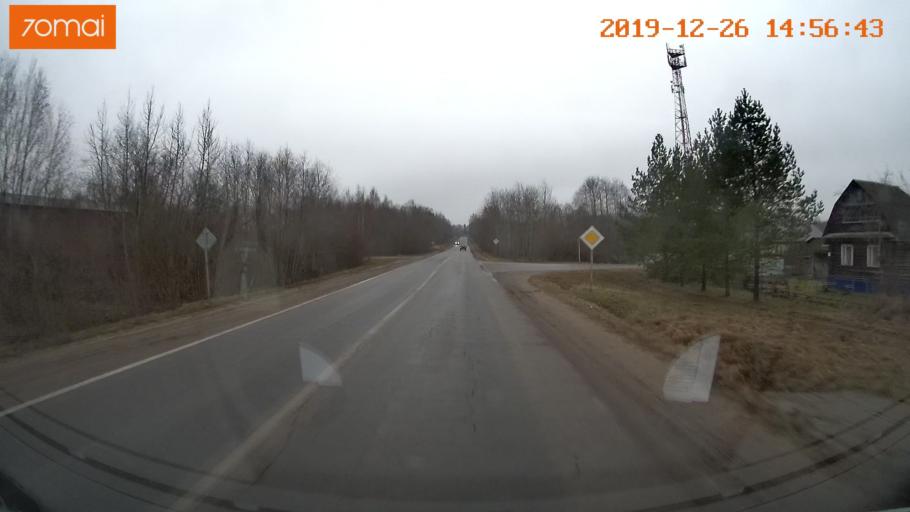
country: RU
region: Jaroslavl
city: Rybinsk
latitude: 58.2898
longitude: 38.8698
